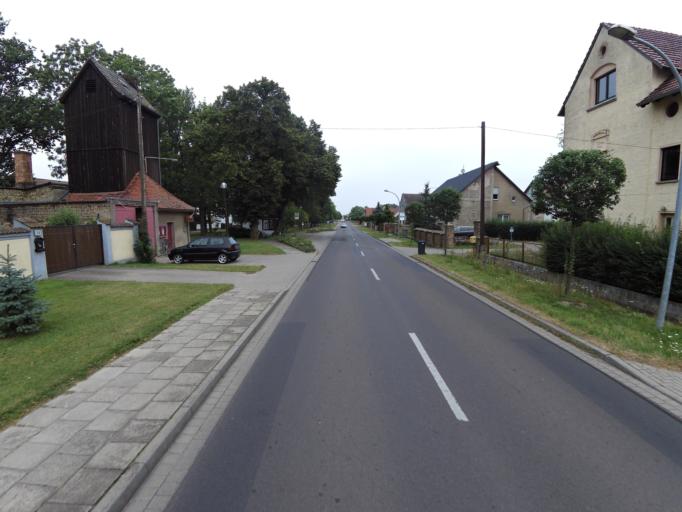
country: DE
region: Brandenburg
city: Zehdenick
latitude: 53.0107
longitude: 13.2882
